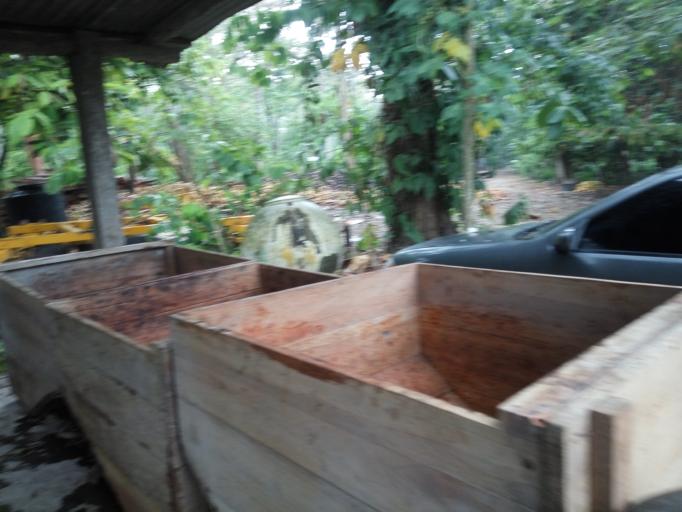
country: MX
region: Tabasco
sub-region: Comalcalco
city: Oriente 2da. Seccion (San Cayetano)
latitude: 18.1825
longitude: -93.2404
